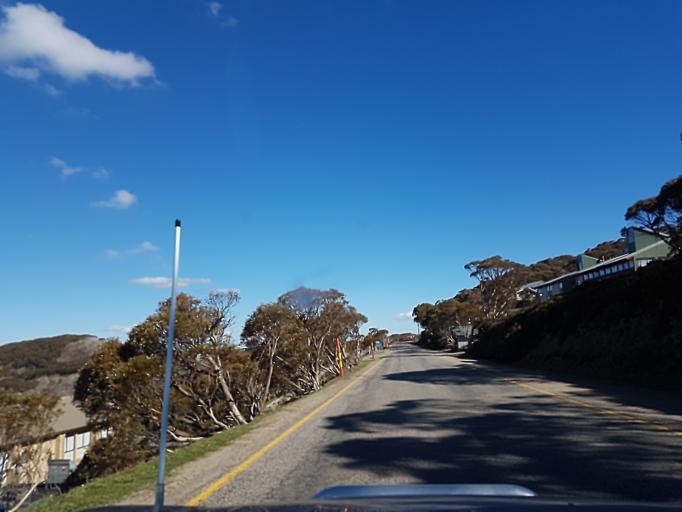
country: AU
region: Victoria
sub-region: Alpine
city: Mount Beauty
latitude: -36.9872
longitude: 147.1480
